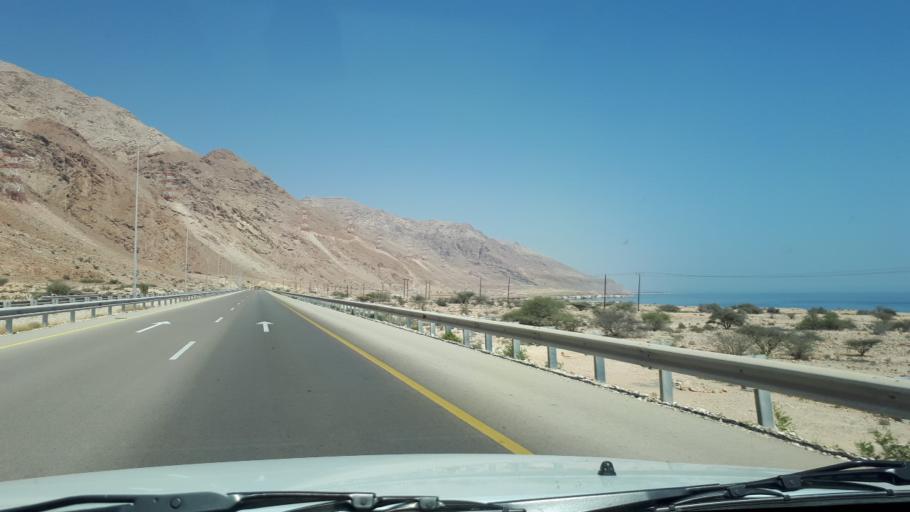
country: OM
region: Ash Sharqiyah
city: Sur
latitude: 22.7572
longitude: 59.2982
